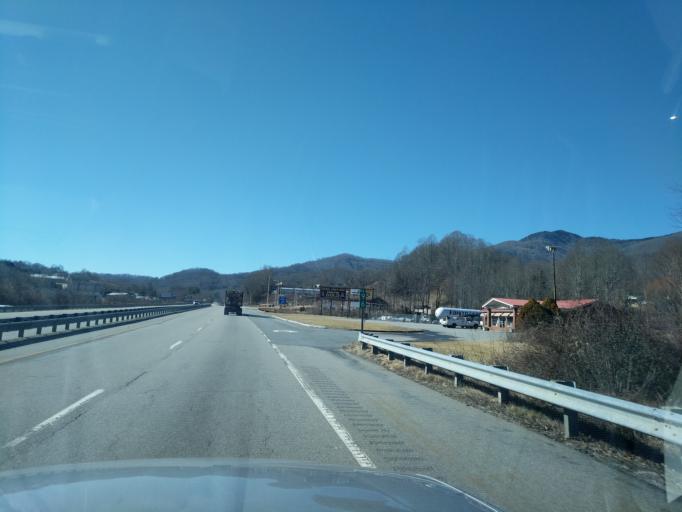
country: US
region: North Carolina
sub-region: Haywood County
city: Hazelwood
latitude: 35.4558
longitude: -83.0495
